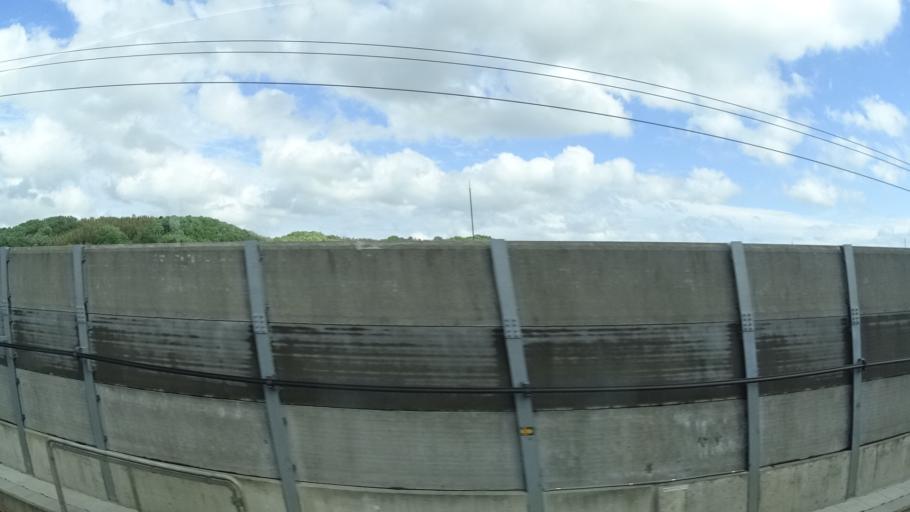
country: JP
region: Ishikawa
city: Kanazawa-shi
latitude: 36.6040
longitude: 136.6811
